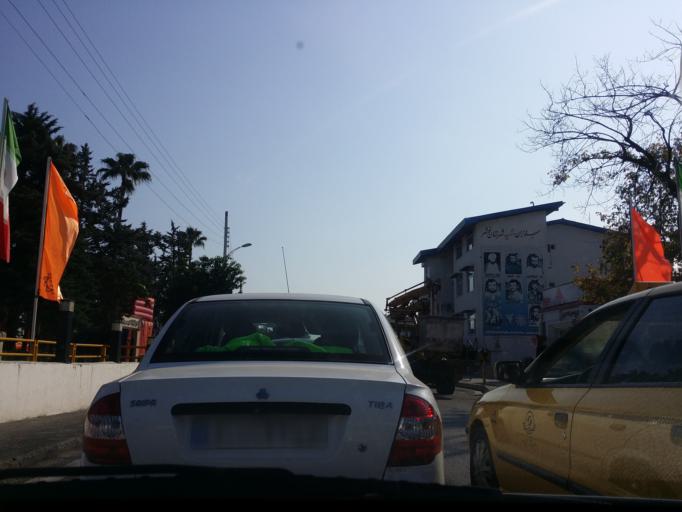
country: IR
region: Mazandaran
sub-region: Nowshahr
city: Nowshahr
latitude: 36.6517
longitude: 51.4992
